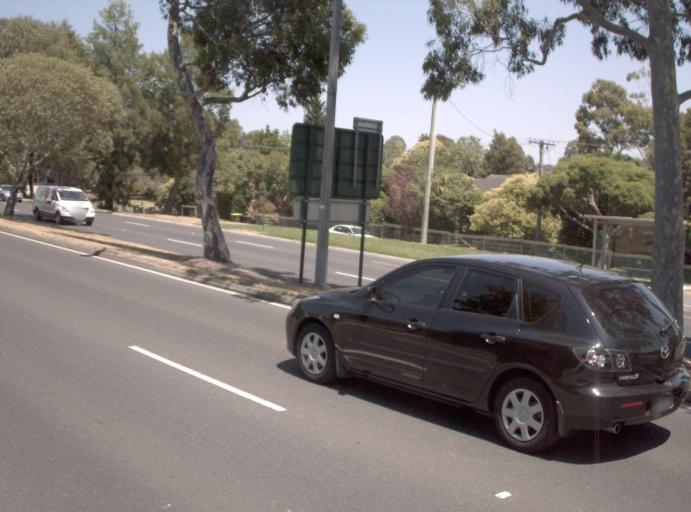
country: AU
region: Victoria
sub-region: Whitehorse
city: Forest Hill
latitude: -37.8373
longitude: 145.1723
